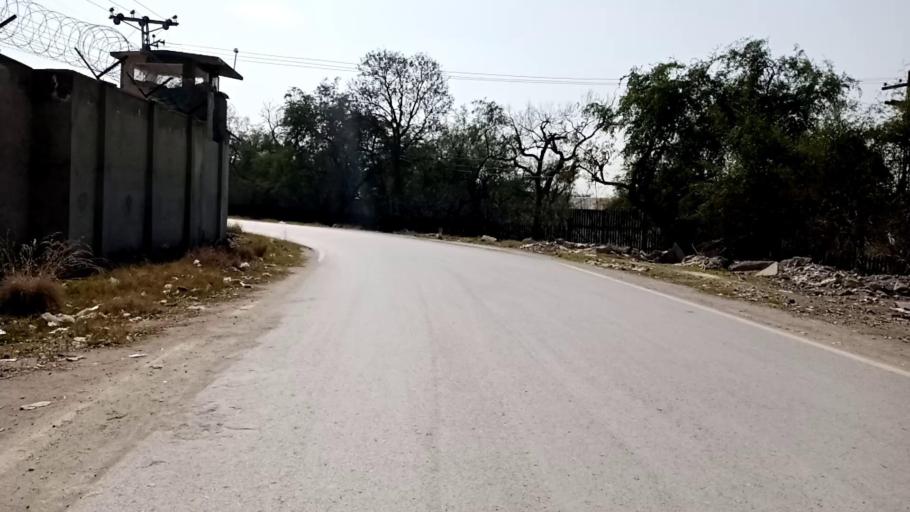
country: PK
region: Khyber Pakhtunkhwa
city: Peshawar
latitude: 33.9920
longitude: 71.5105
